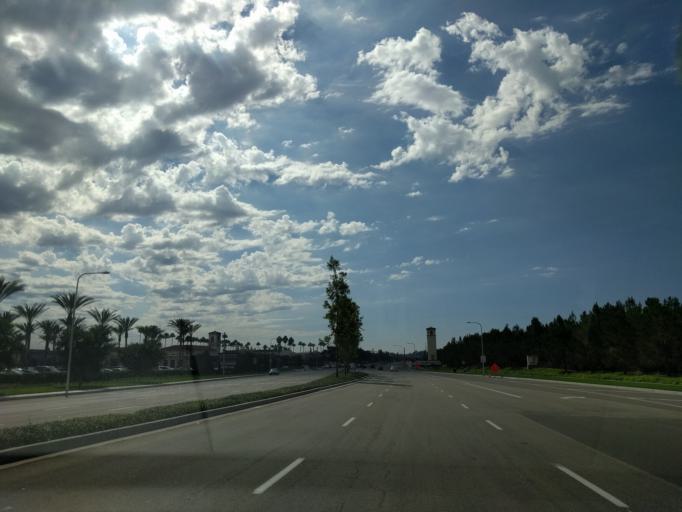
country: US
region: California
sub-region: Orange County
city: Laguna Woods
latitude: 33.6462
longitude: -117.7461
